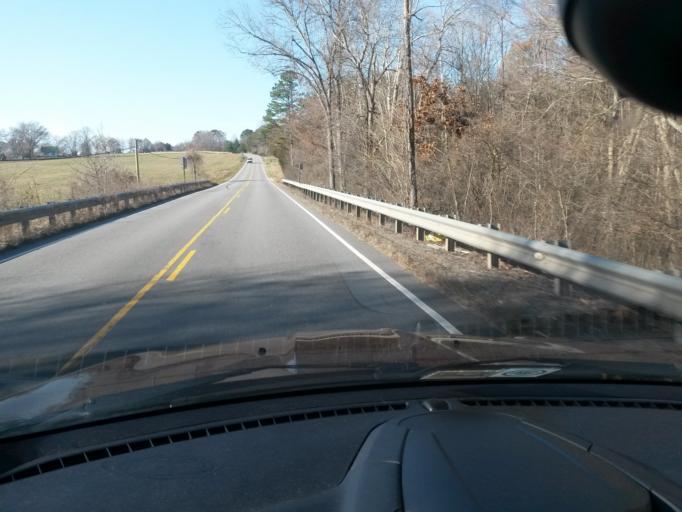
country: US
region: Virginia
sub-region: Charlotte County
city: Charlotte Court House
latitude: 37.1239
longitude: -78.6570
